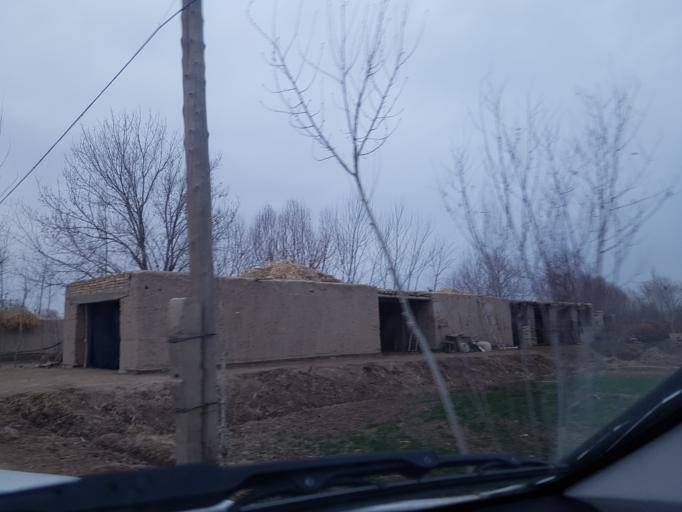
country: TM
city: Akdepe
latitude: 41.9835
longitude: 59.4697
